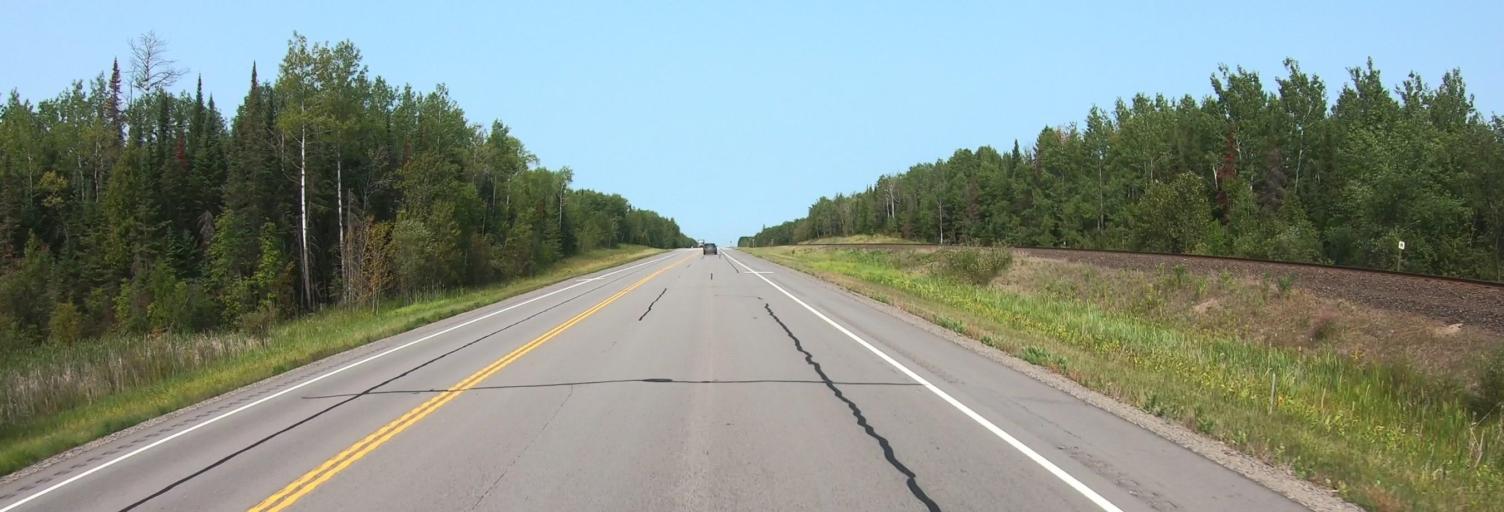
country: CA
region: Ontario
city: Fort Frances
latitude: 48.4600
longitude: -93.2850
